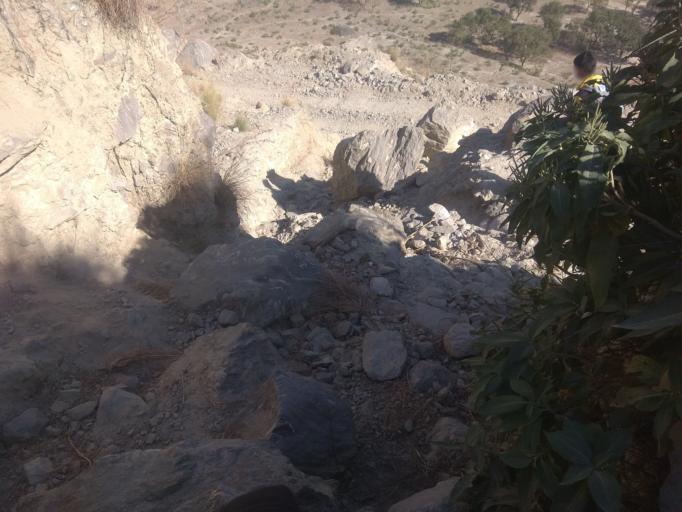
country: NP
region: Mid Western
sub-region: Karnali Zone
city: Jumla
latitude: 29.2965
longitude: 81.7459
